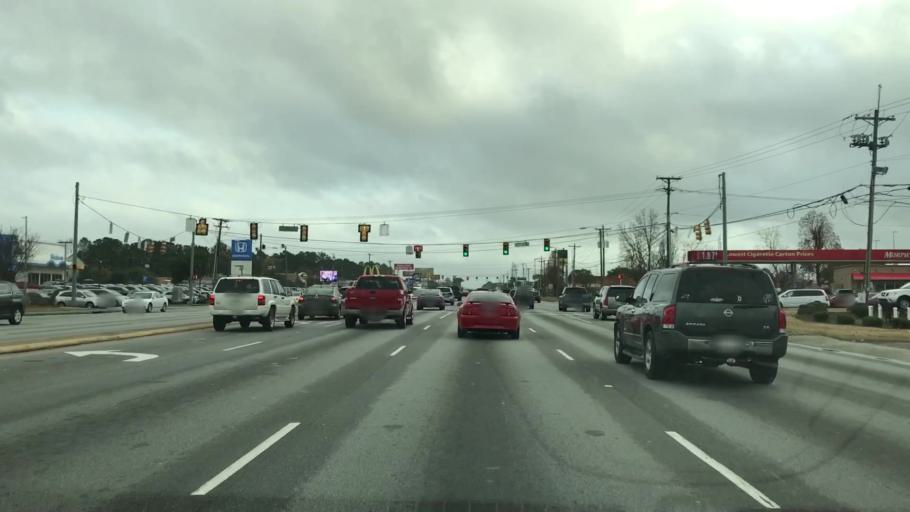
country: US
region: South Carolina
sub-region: Berkeley County
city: Goose Creek
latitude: 32.9657
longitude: -80.0444
